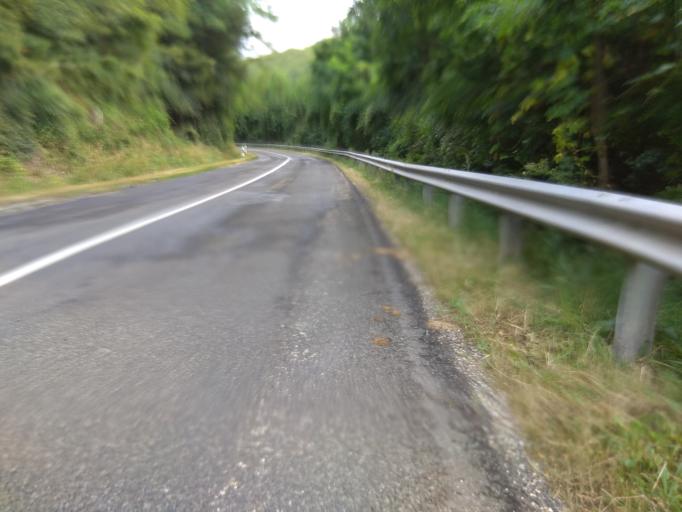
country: HU
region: Heves
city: Tarnalelesz
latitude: 48.0546
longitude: 20.2140
